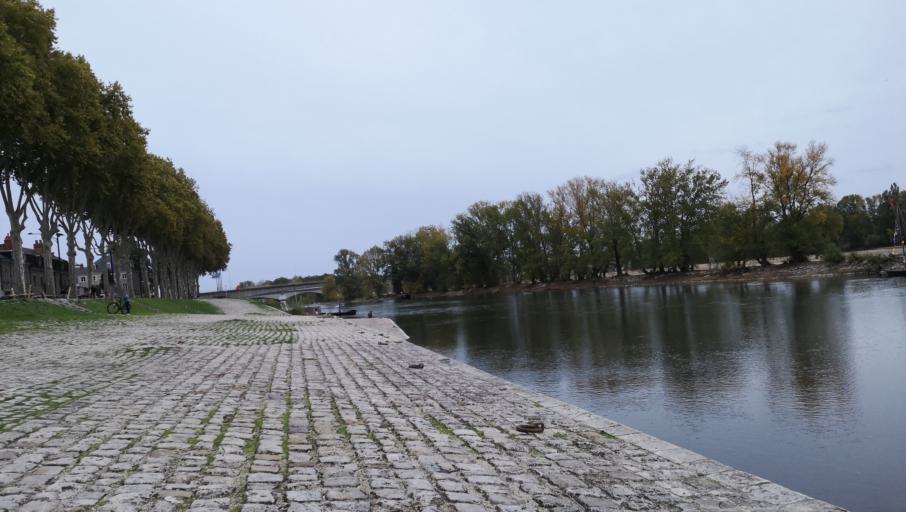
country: FR
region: Centre
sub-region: Departement du Loiret
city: Saint-Jean-le-Blanc
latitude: 47.8978
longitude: 1.9134
